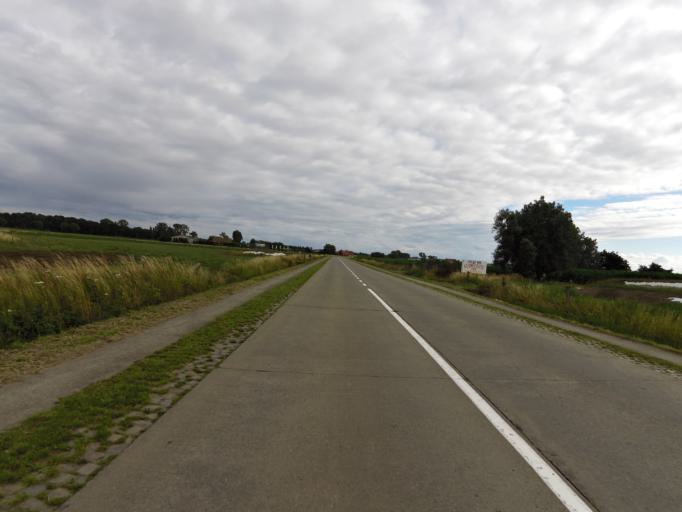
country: BE
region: Flanders
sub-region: Provincie West-Vlaanderen
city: Koekelare
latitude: 51.1142
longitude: 2.9920
